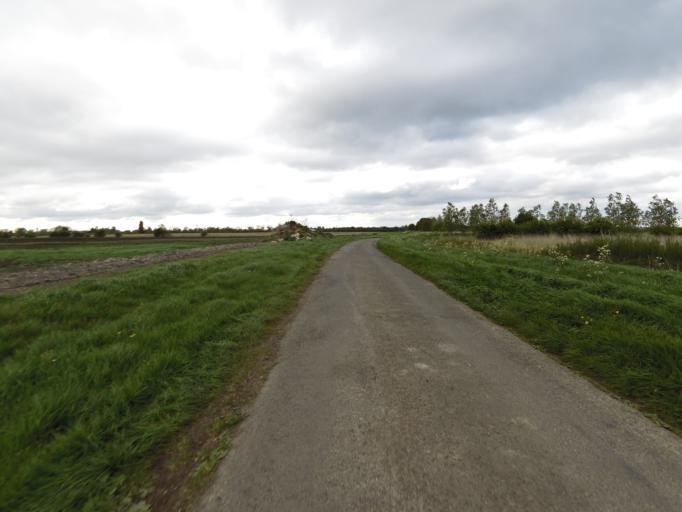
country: GB
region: England
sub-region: Cambridgeshire
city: Bottisham
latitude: 52.2716
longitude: 0.2762
